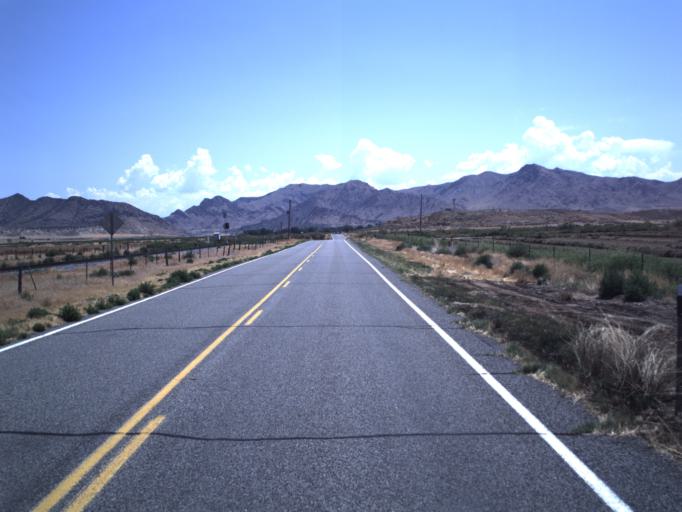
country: US
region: Utah
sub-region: Millard County
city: Delta
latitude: 39.5330
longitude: -112.3275
